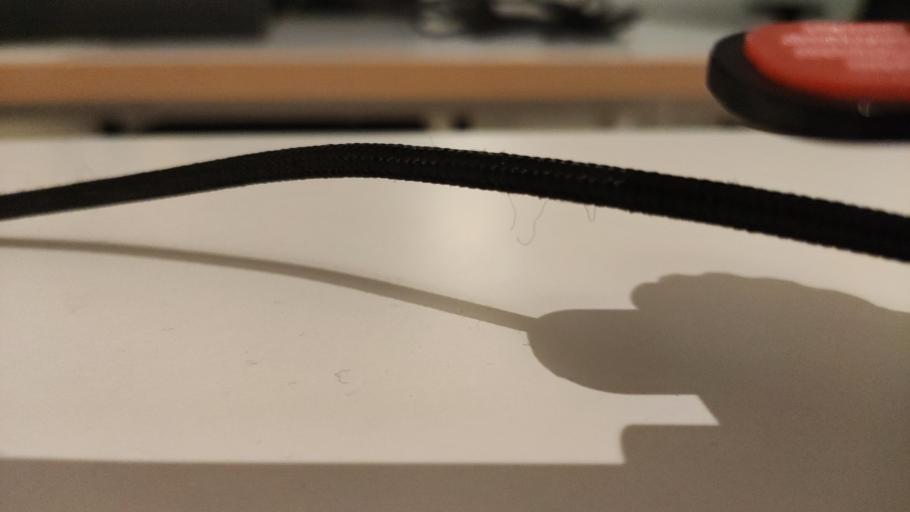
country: RU
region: Moskovskaya
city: Malaya Dubna
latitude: 55.8478
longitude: 38.9643
